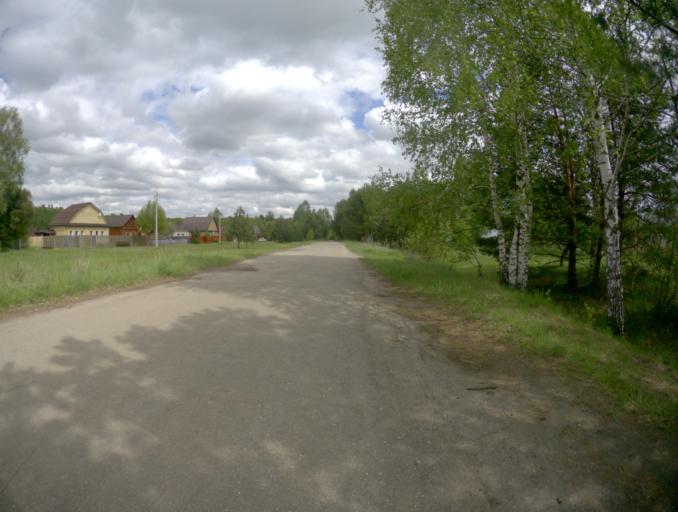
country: RU
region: Rjazan
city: Gus'-Zheleznyy
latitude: 55.1181
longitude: 40.9275
